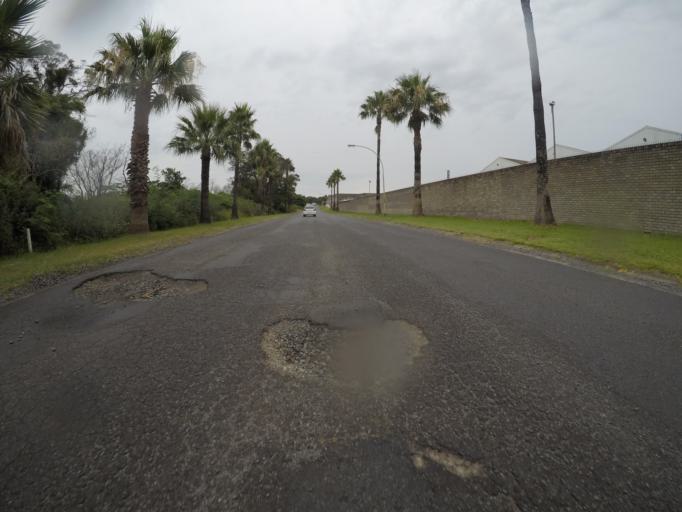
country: ZA
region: Eastern Cape
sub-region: Buffalo City Metropolitan Municipality
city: East London
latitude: -32.9718
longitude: 27.8185
